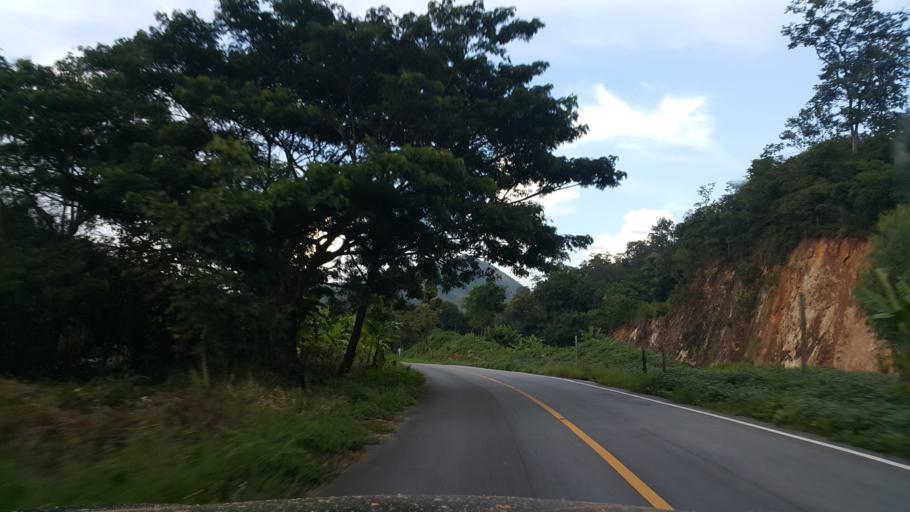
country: TH
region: Mae Hong Son
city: Mae Hi
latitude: 19.2376
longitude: 98.4492
